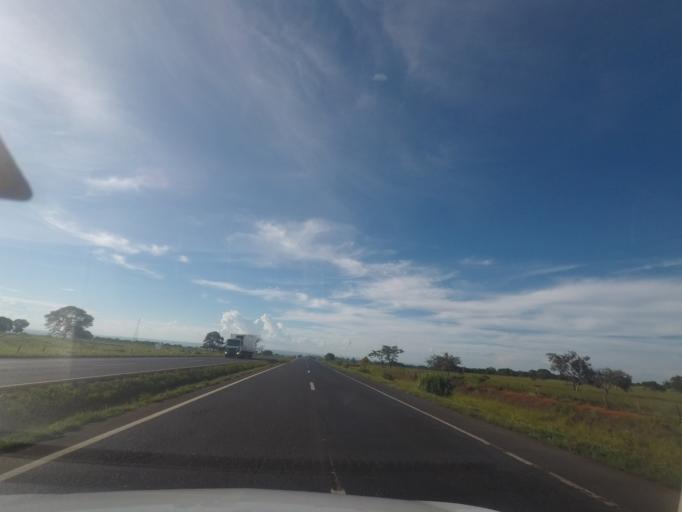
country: BR
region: Minas Gerais
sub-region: Centralina
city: Centralina
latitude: -18.6706
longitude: -49.1611
